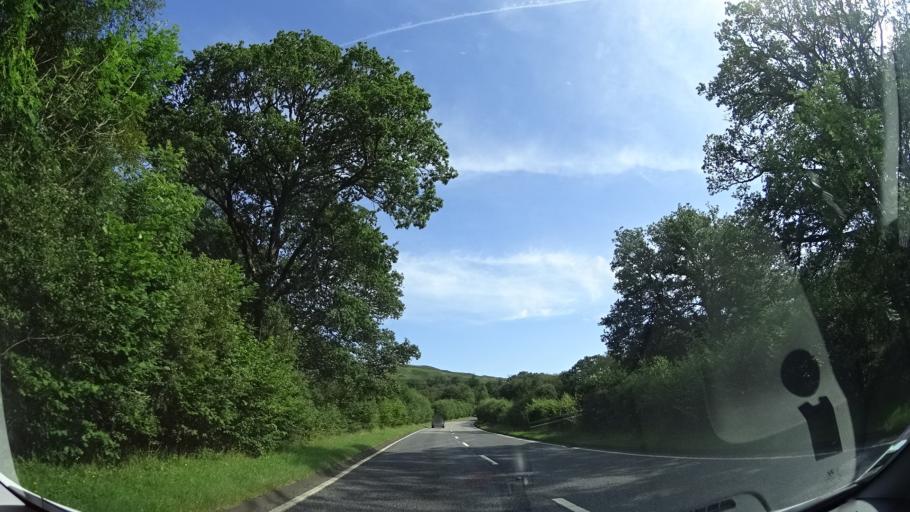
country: GB
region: Scotland
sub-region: Argyll and Bute
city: Garelochhead
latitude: 56.3473
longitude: -4.7026
